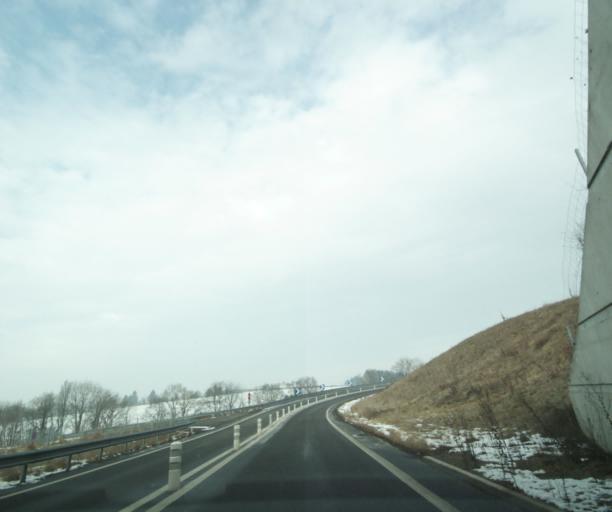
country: FR
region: Rhone-Alpes
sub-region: Departement de la Loire
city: Bussieres
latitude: 45.8514
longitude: 4.2234
